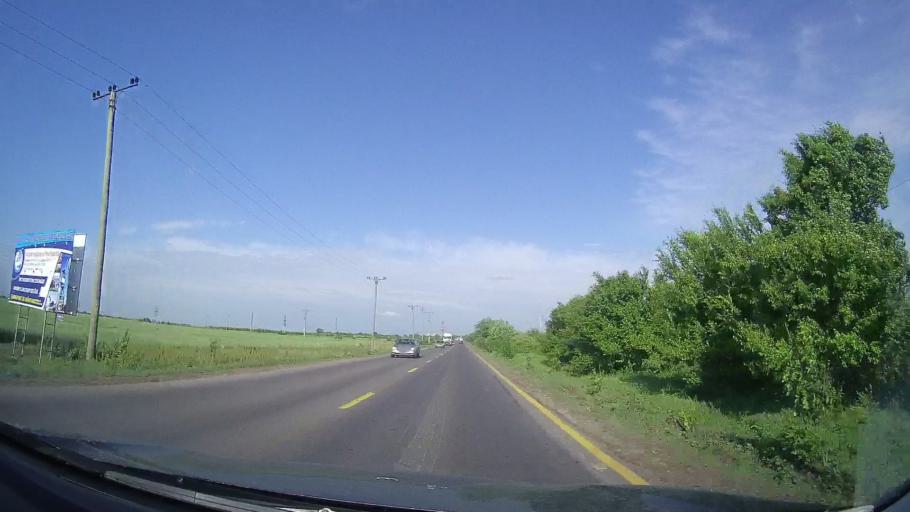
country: RO
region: Ilfov
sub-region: Comuna Vidra
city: Sintesti
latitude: 44.3353
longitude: 26.1231
